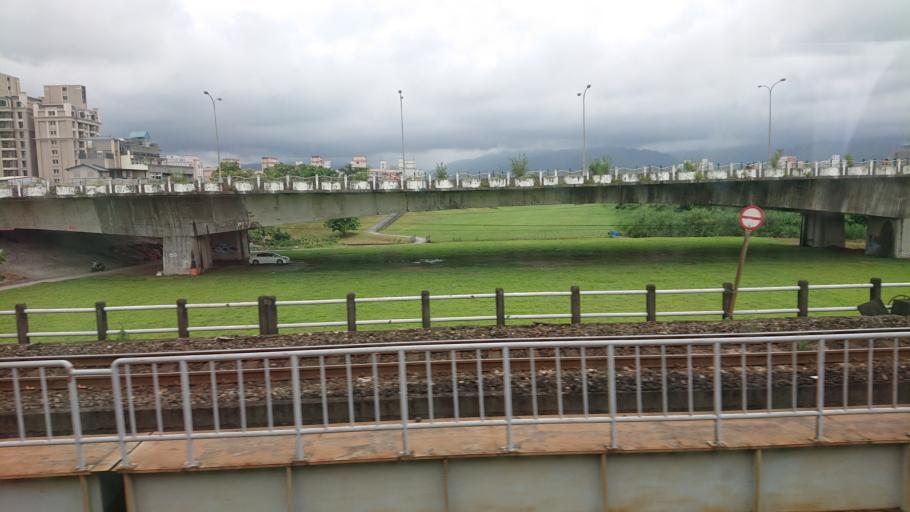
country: TW
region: Taiwan
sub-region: Yilan
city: Yilan
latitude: 24.7628
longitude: 121.7615
